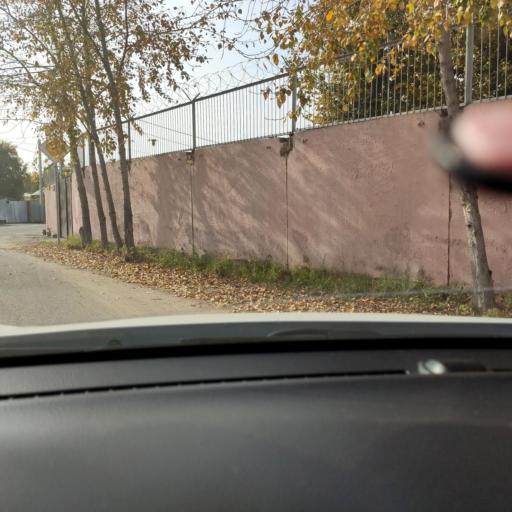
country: RU
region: Tatarstan
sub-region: Gorod Kazan'
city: Kazan
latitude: 55.7391
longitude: 49.1723
